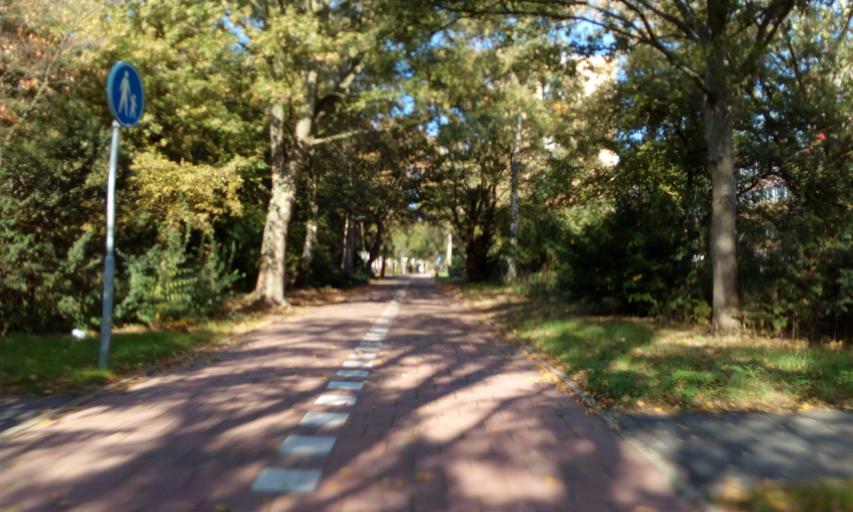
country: NL
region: South Holland
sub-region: Gemeente Vlaardingen
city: Vlaardingen
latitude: 51.9243
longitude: 4.3498
